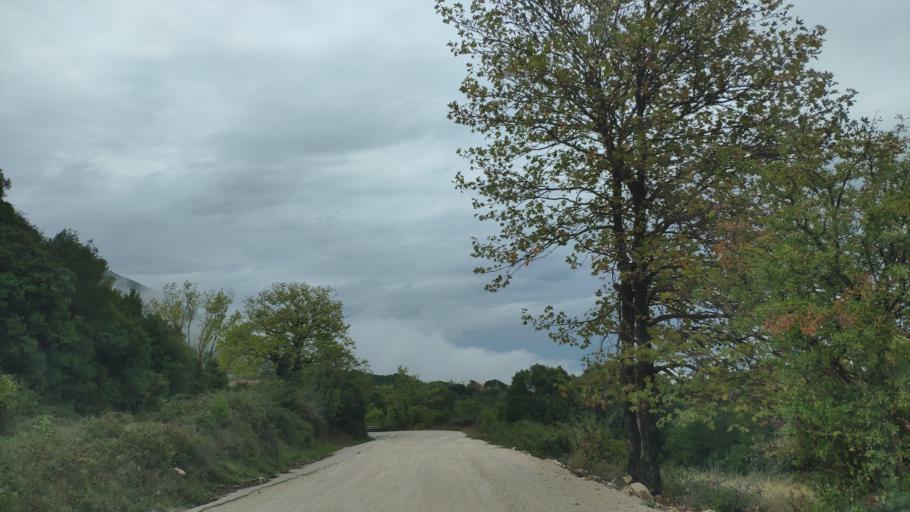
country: GR
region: Epirus
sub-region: Nomos Thesprotias
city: Paramythia
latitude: 39.4590
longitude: 20.6786
